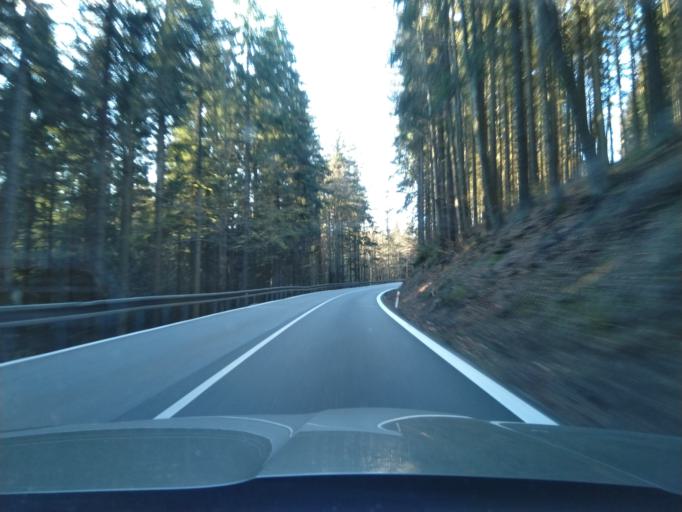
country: CZ
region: Jihocesky
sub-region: Okres Prachatice
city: Vimperk
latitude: 48.9912
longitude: 13.7693
